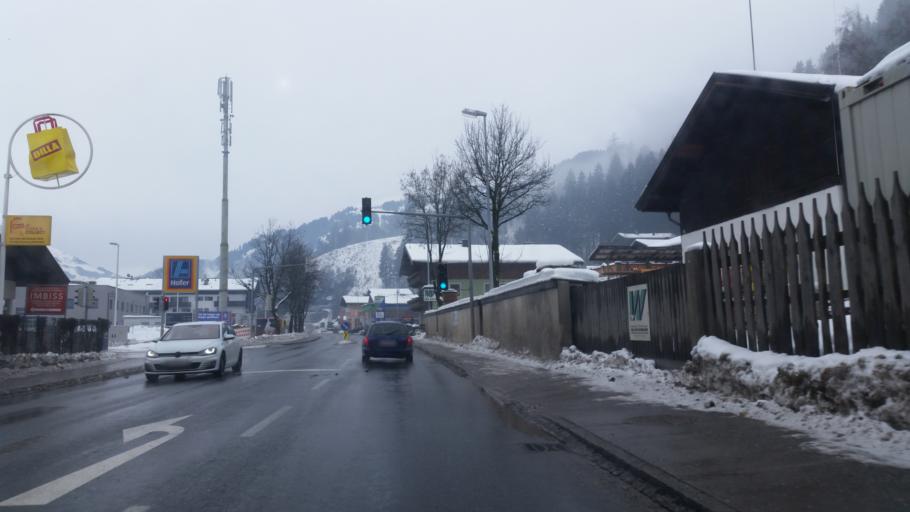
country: AT
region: Tyrol
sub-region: Politischer Bezirk Kitzbuhel
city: Kitzbuhel
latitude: 47.4576
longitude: 12.3863
